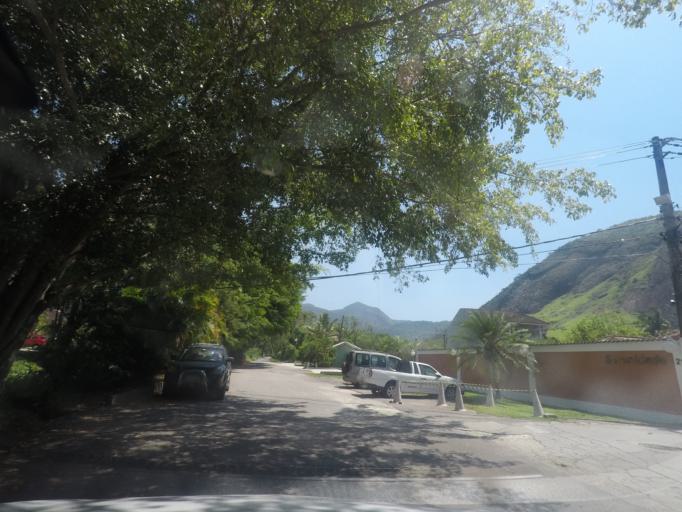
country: BR
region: Rio de Janeiro
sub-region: Nilopolis
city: Nilopolis
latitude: -22.9915
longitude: -43.4561
